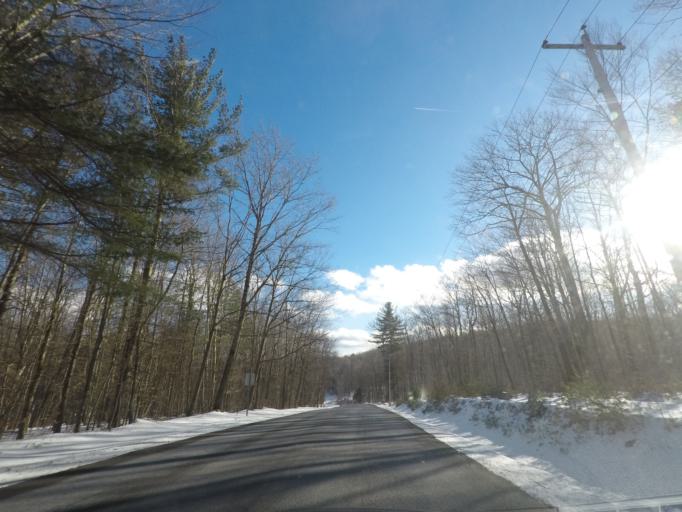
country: US
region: New York
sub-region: Rensselaer County
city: Hoosick Falls
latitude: 42.7948
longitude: -73.4013
